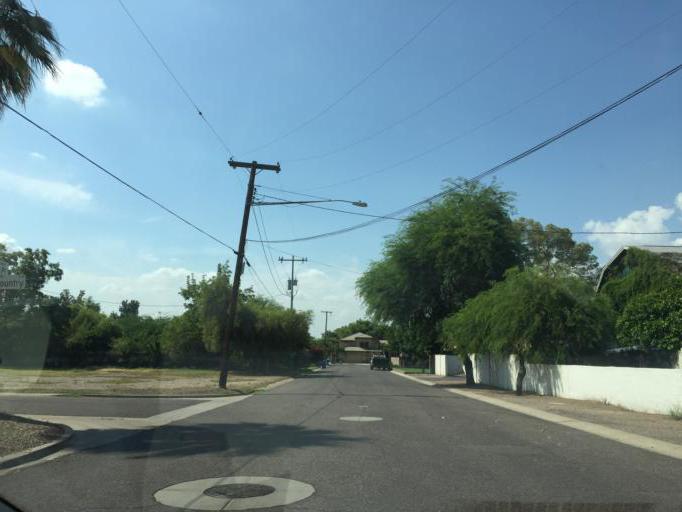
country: US
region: Arizona
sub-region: Maricopa County
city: Phoenix
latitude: 33.5342
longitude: -112.0504
